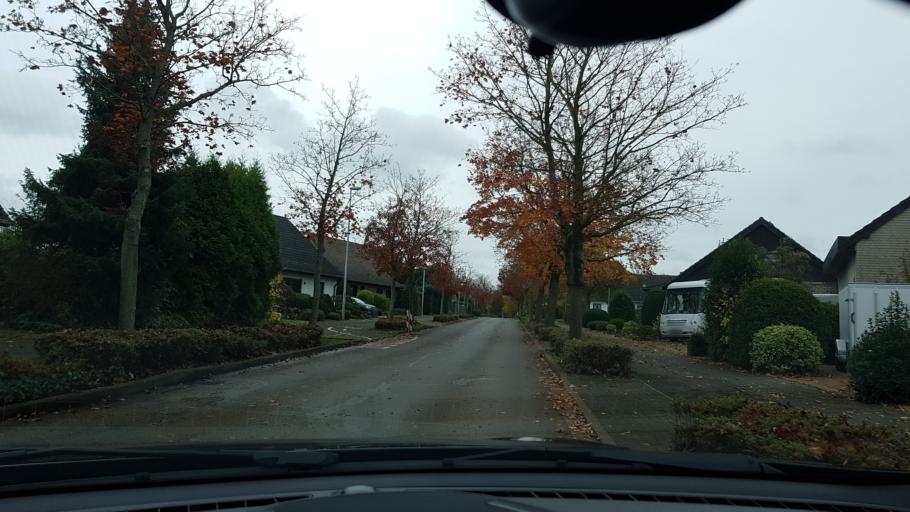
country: DE
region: North Rhine-Westphalia
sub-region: Regierungsbezirk Koln
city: Bedburg
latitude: 51.0000
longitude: 6.5557
